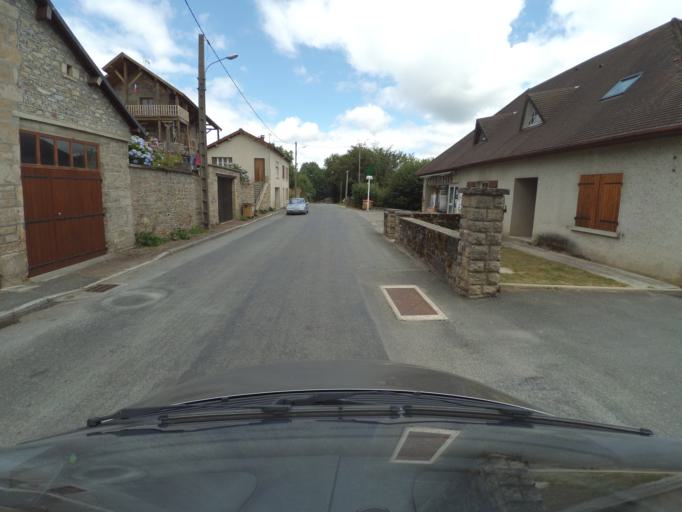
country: FR
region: Limousin
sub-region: Departement de la Haute-Vienne
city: Peyrat-le-Chateau
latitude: 45.8419
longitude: 1.9099
